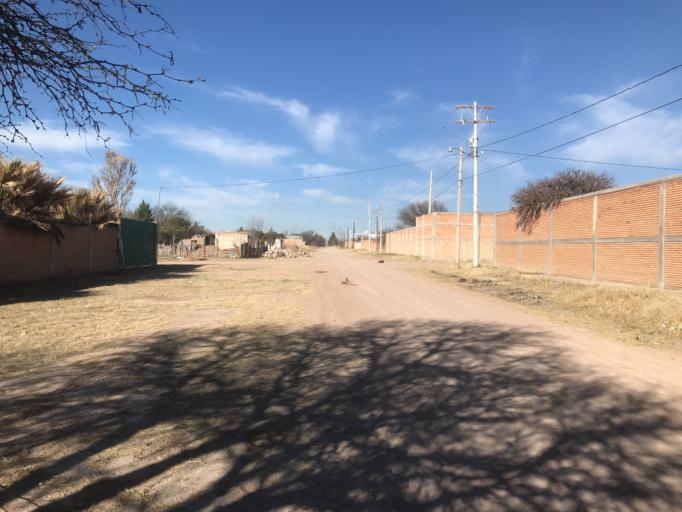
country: MX
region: Durango
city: Victoria de Durango
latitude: 24.0193
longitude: -104.5839
